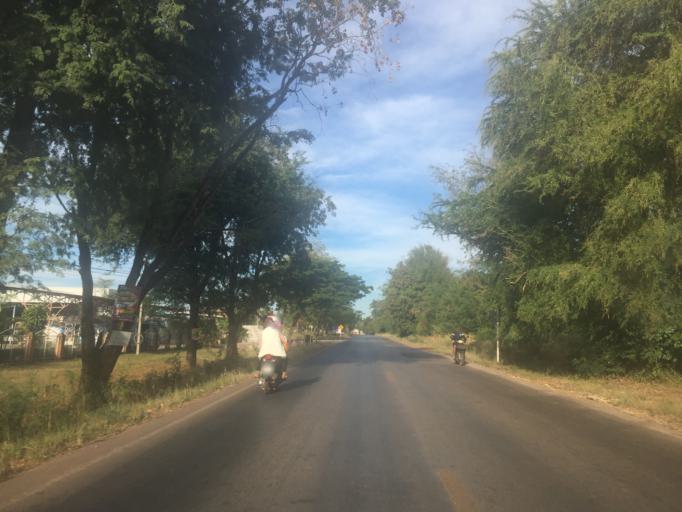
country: TH
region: Changwat Udon Thani
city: Si That
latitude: 16.9724
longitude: 103.2312
